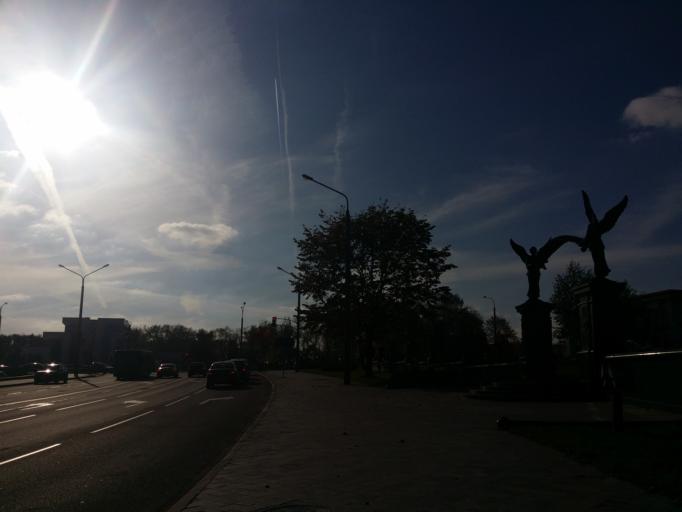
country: BY
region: Minsk
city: Minsk
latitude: 53.9232
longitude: 27.5498
